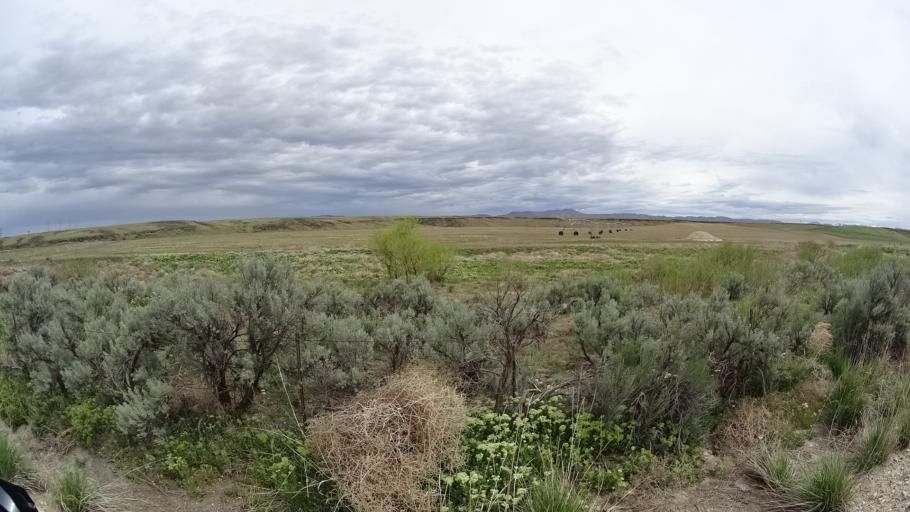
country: US
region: Idaho
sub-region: Ada County
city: Boise
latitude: 43.3890
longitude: -115.9842
